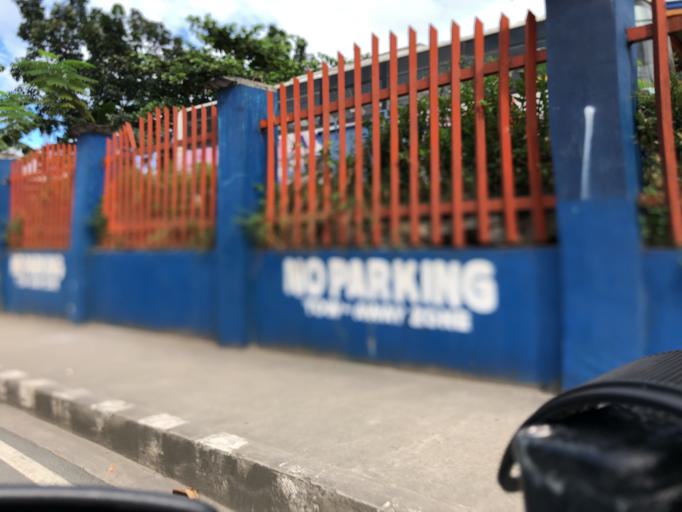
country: PH
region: Central Luzon
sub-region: Province of Bulacan
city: San Jose del Monte
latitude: 14.7506
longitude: 121.0532
